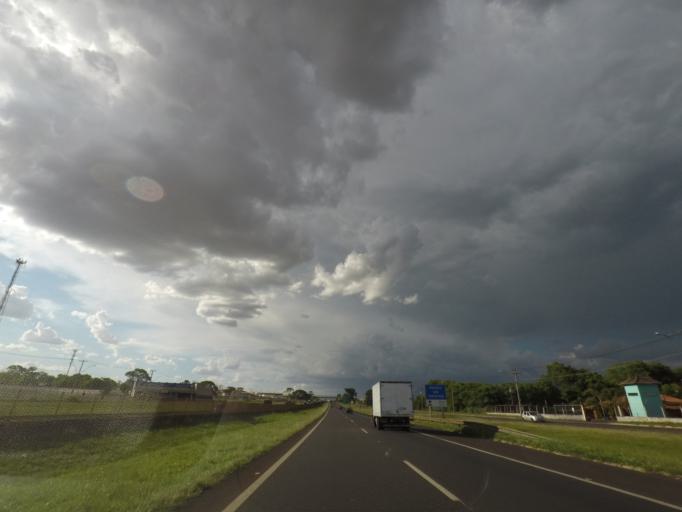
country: BR
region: Sao Paulo
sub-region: Ribeirao Preto
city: Ribeirao Preto
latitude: -21.1326
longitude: -47.7659
